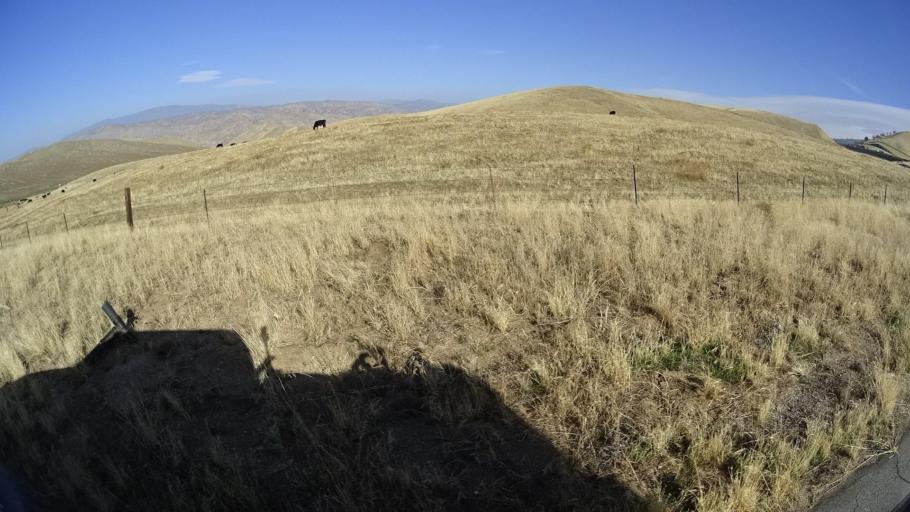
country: US
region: California
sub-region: Kern County
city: Bear Valley Springs
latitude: 35.2736
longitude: -118.6888
